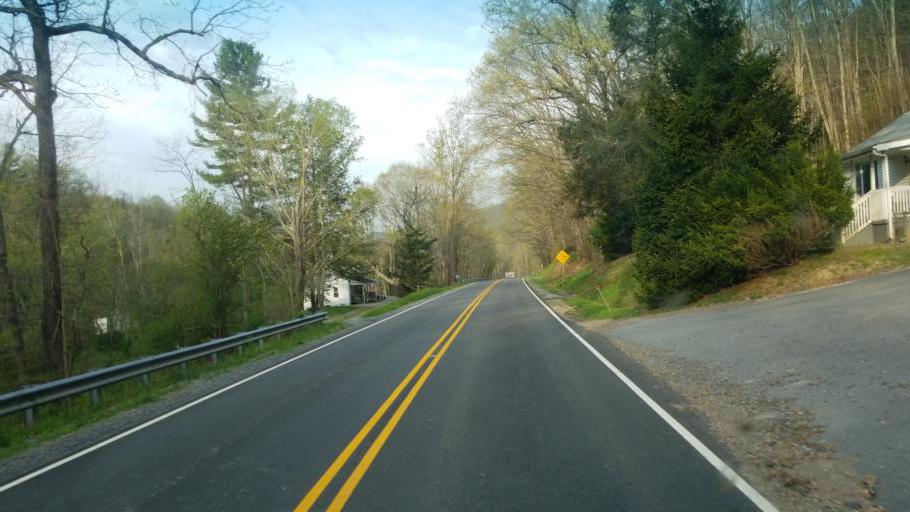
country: US
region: Virginia
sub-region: Smyth County
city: Atkins
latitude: 36.8145
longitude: -81.4553
